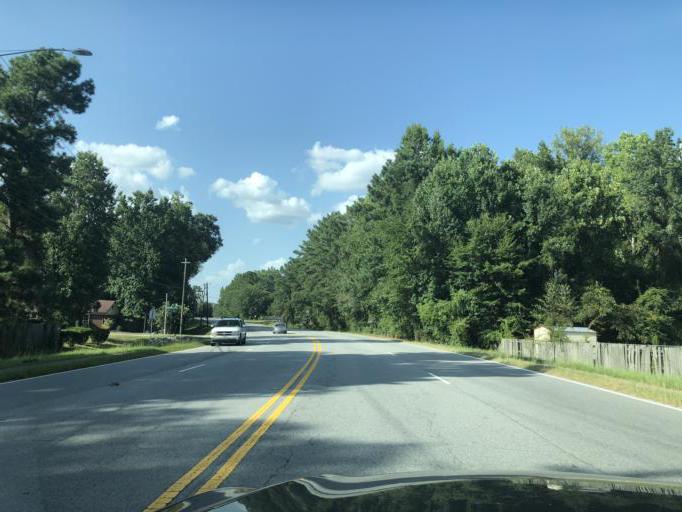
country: US
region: Georgia
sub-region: Muscogee County
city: Columbus
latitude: 32.4853
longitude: -84.8967
